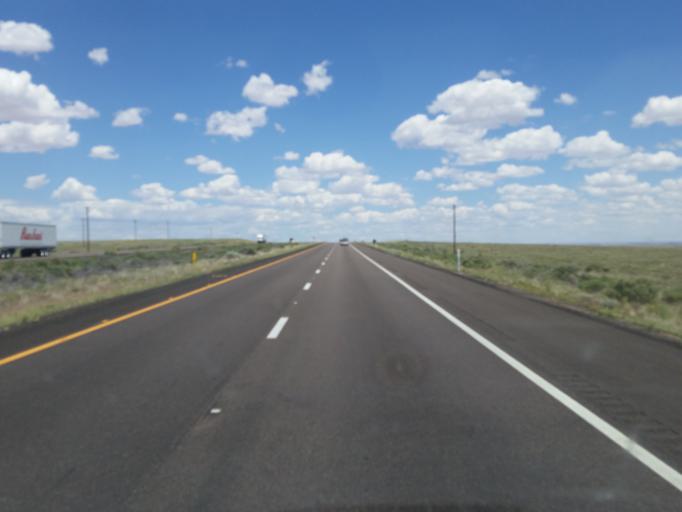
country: US
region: Arizona
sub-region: Navajo County
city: Holbrook
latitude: 34.9865
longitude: -110.0208
